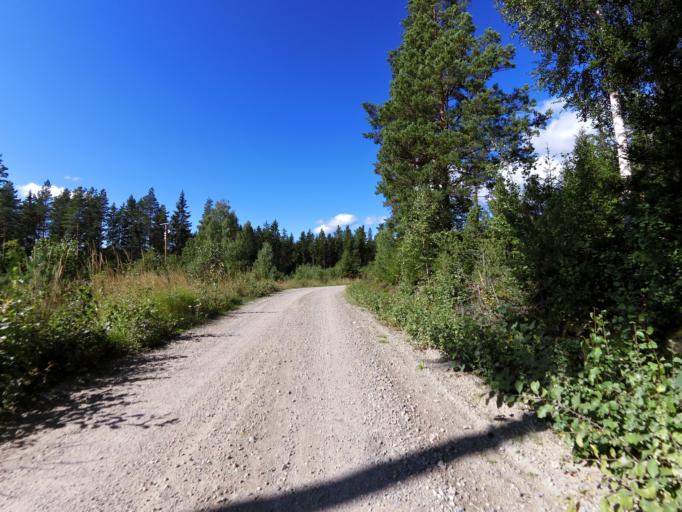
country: SE
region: Gaevleborg
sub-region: Gavle Kommun
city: Valbo
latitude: 60.7787
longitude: 16.9139
